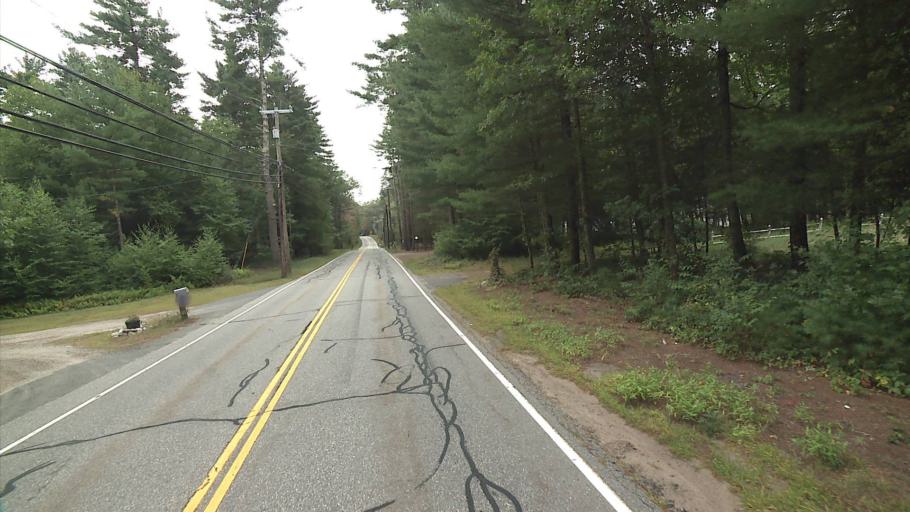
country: US
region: Connecticut
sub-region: Tolland County
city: Storrs
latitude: 41.8418
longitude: -72.2723
